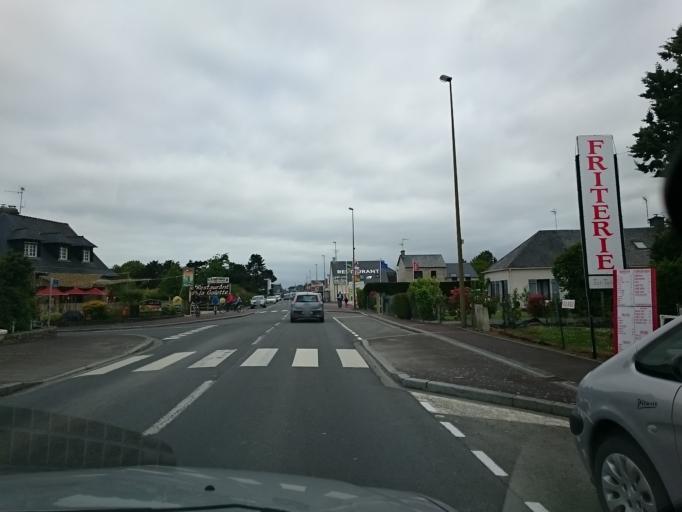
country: FR
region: Lower Normandy
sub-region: Departement de la Manche
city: Pontorson
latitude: 48.5956
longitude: -1.5123
